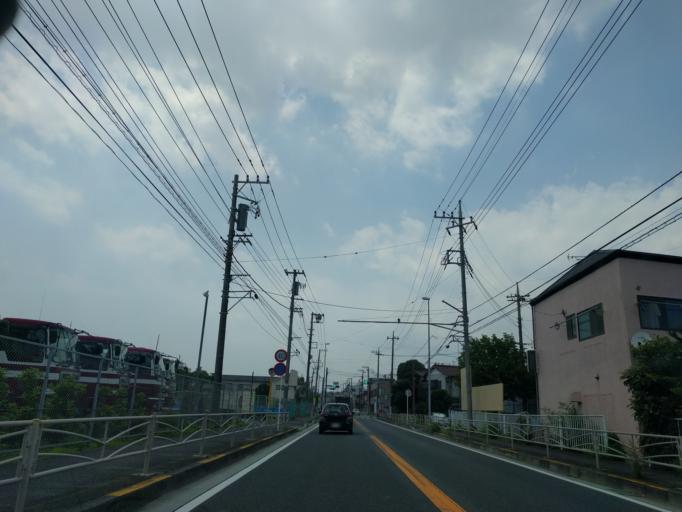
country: JP
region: Kanagawa
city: Minami-rinkan
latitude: 35.4891
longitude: 139.5170
